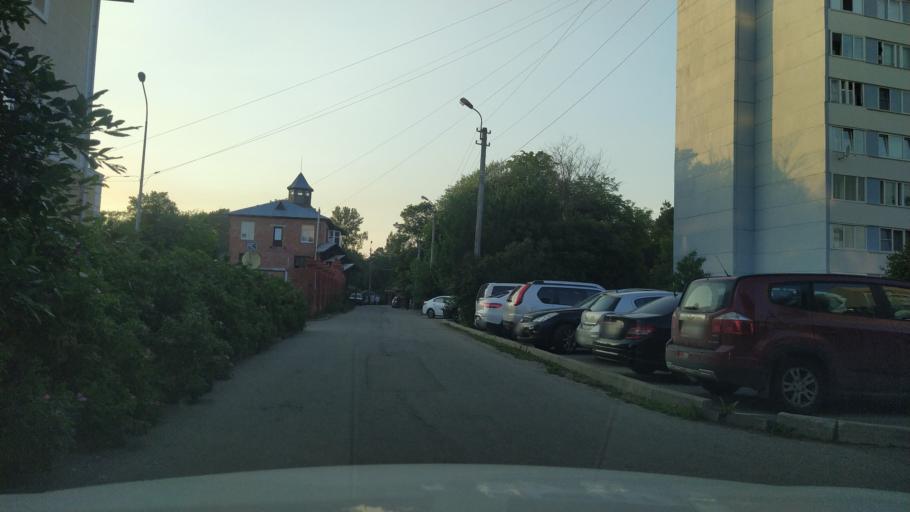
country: RU
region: St.-Petersburg
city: Sestroretsk
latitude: 60.0918
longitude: 29.9481
